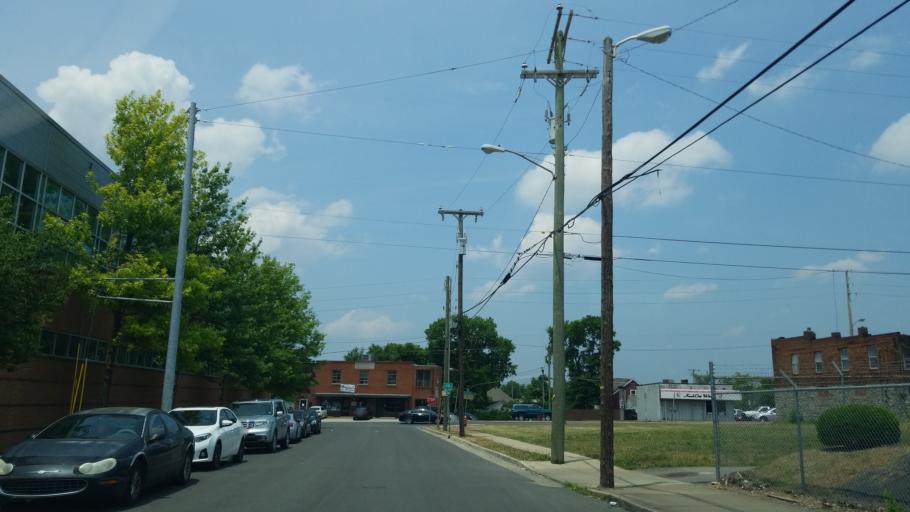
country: US
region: Tennessee
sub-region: Davidson County
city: Nashville
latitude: 36.1702
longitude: -86.8009
